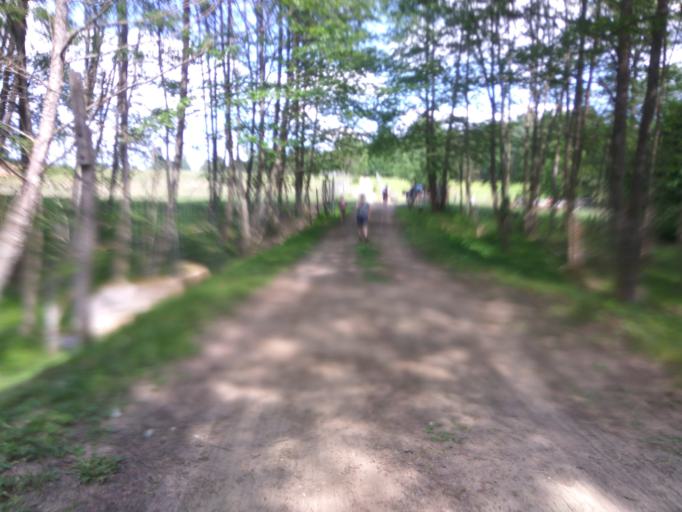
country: LV
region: Kuldigas Rajons
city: Kuldiga
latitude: 56.8863
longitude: 21.9277
